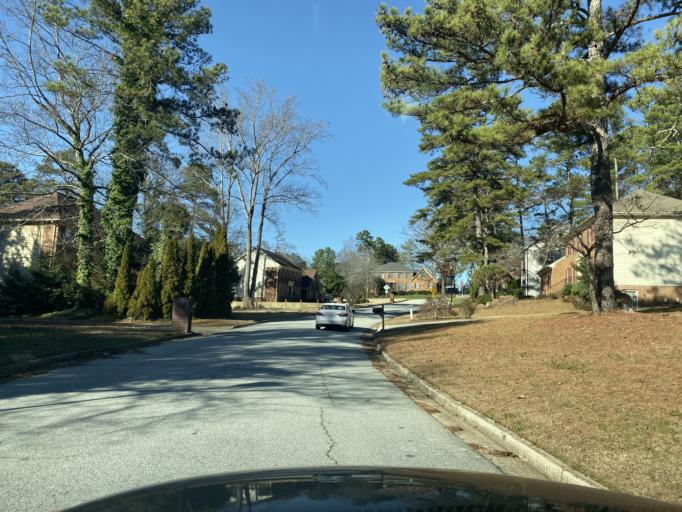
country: US
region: Georgia
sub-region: DeKalb County
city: Pine Mountain
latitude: 33.6809
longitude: -84.1601
